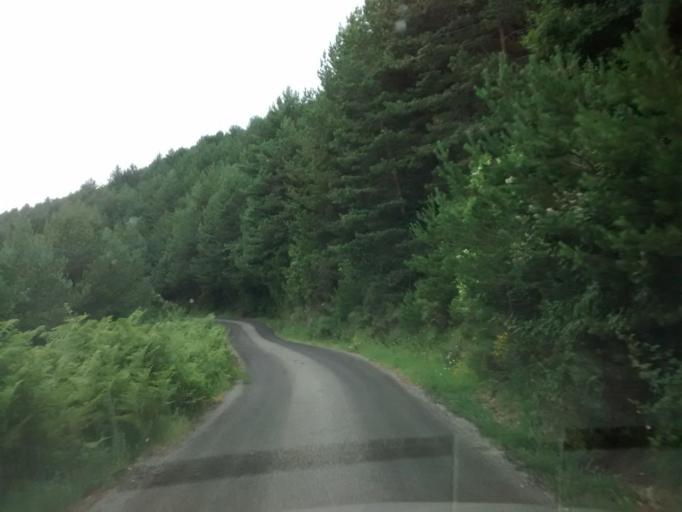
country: ES
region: Aragon
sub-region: Provincia de Huesca
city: Puertolas
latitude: 42.5652
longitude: 0.1401
